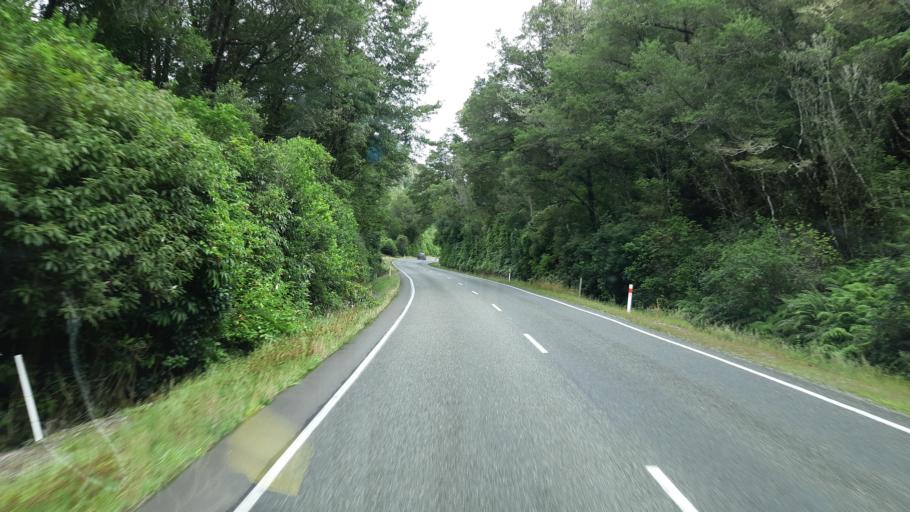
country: NZ
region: West Coast
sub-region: Buller District
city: Westport
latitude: -41.7936
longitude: 172.2167
